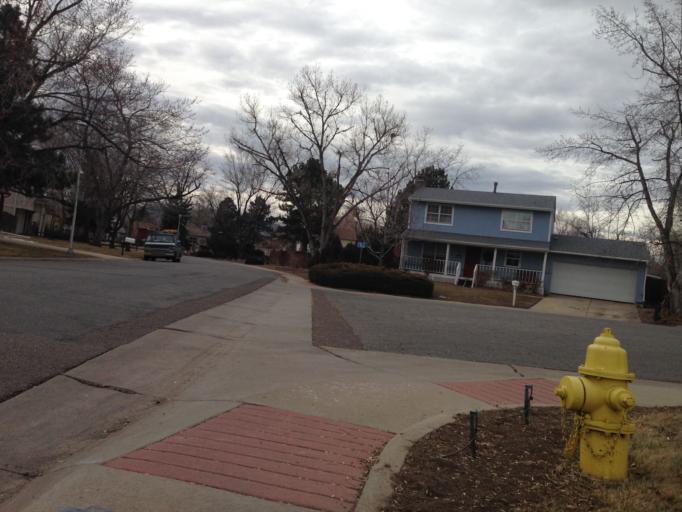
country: US
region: Colorado
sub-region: Adams County
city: Westminster
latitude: 39.8554
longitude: -105.0634
